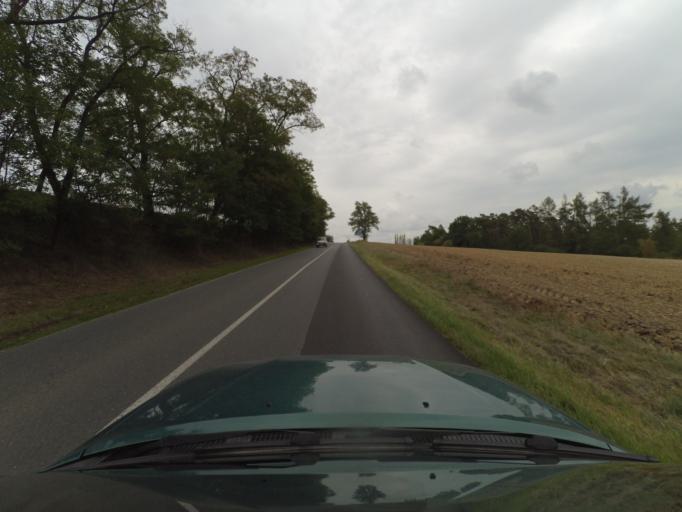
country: CZ
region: Plzensky
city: Kozlany
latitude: 49.9989
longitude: 13.5666
